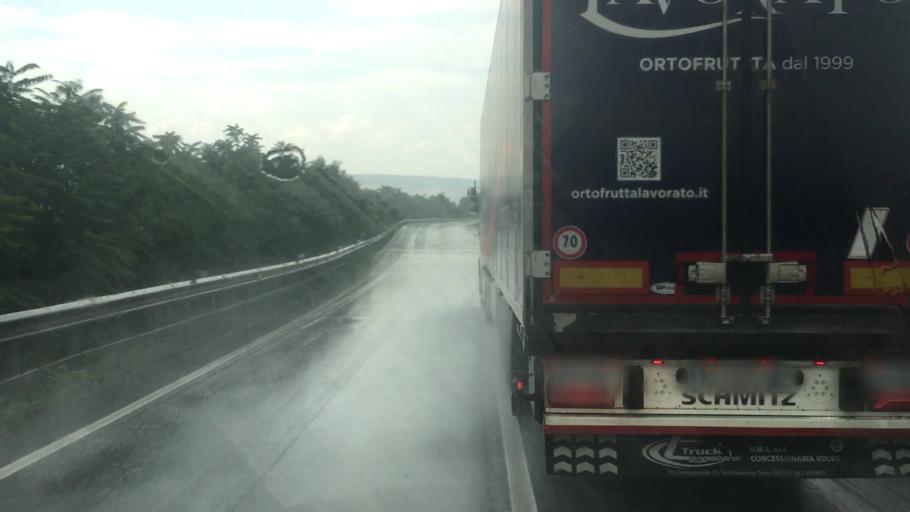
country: IT
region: Basilicate
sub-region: Provincia di Matera
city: Matera
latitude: 40.6279
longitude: 16.5902
